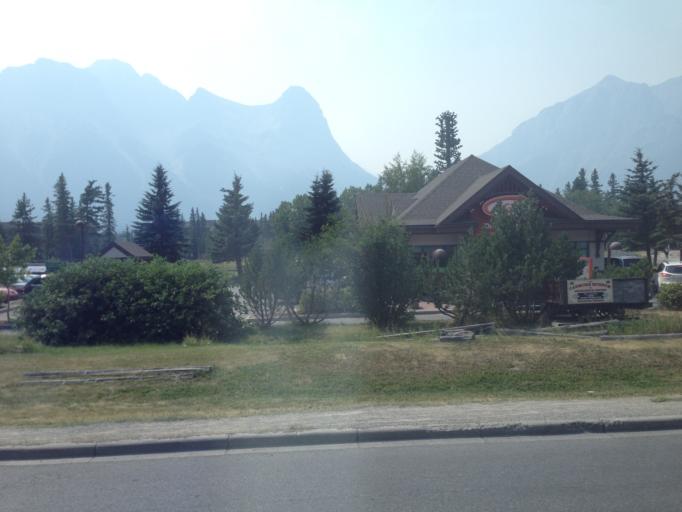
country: CA
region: Alberta
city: Canmore
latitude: 51.0879
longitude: -115.3474
